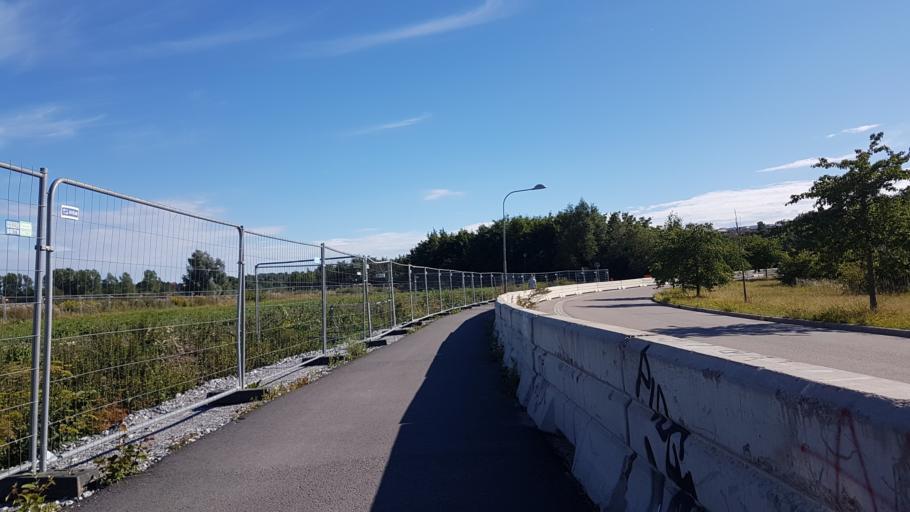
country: SE
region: Stockholm
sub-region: Stockholms Kommun
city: Arsta
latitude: 59.2930
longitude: 18.0403
